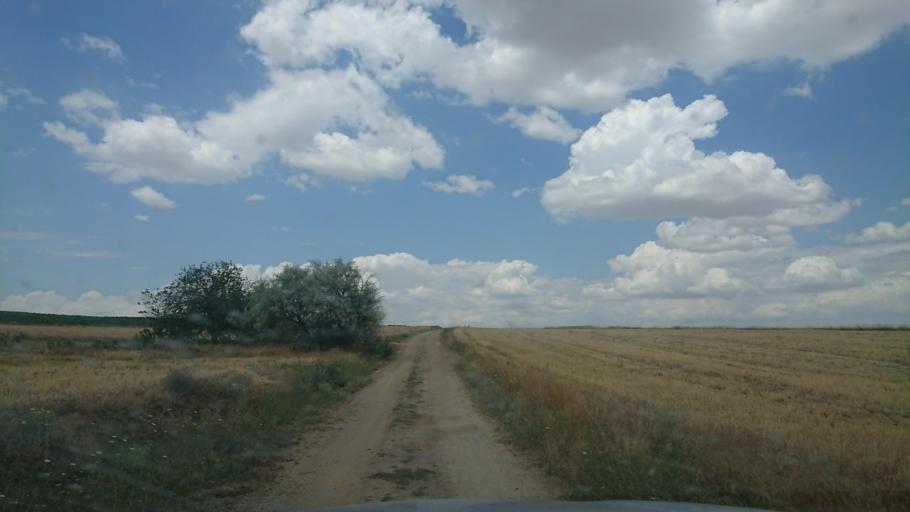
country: TR
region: Aksaray
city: Agacoren
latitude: 38.8950
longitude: 33.8826
